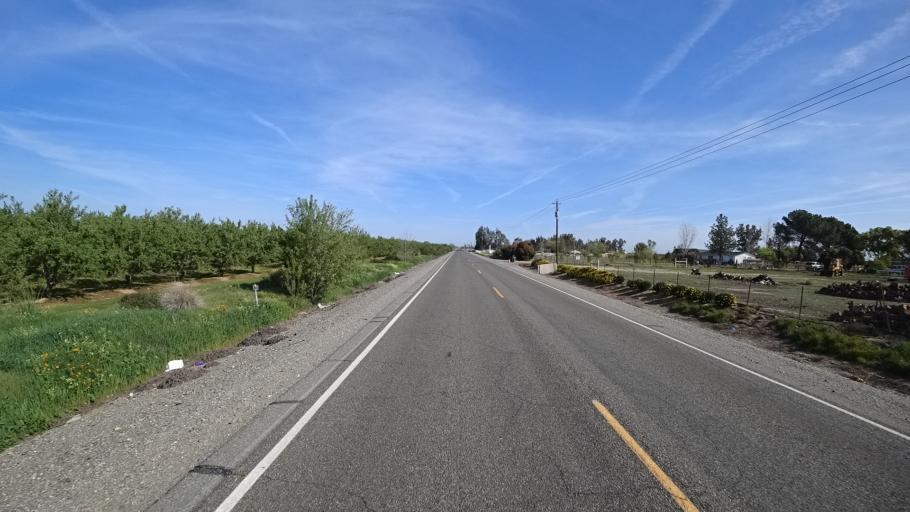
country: US
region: California
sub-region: Glenn County
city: Willows
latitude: 39.6331
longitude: -122.1974
